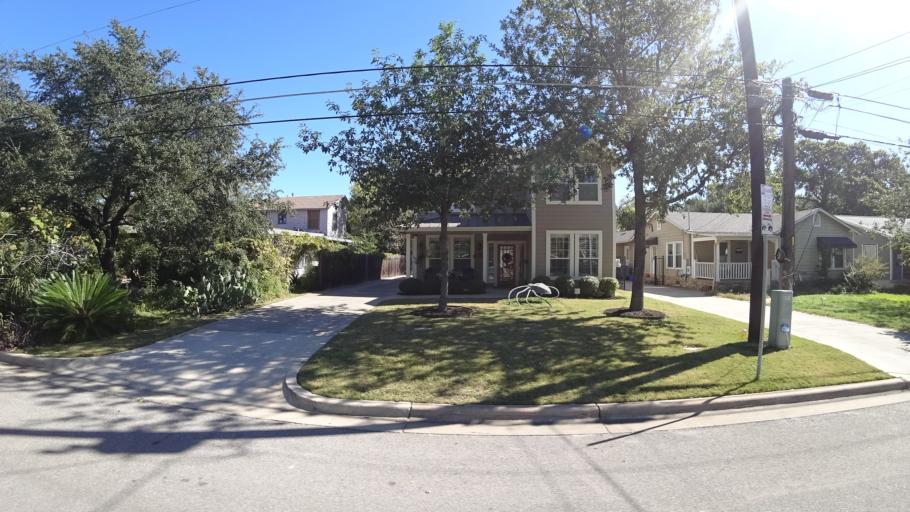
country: US
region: Texas
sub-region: Travis County
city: Austin
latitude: 30.3290
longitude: -97.7414
